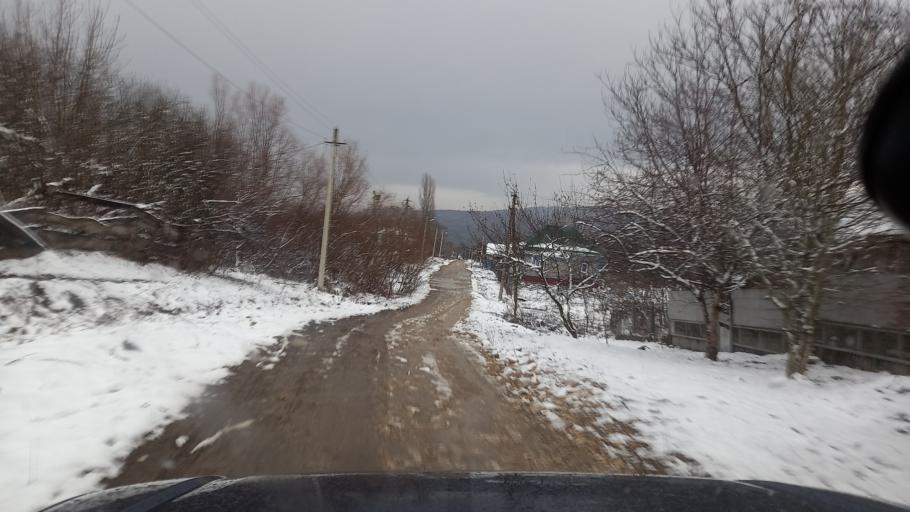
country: RU
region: Adygeya
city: Abadzekhskaya
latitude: 44.3564
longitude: 40.4101
